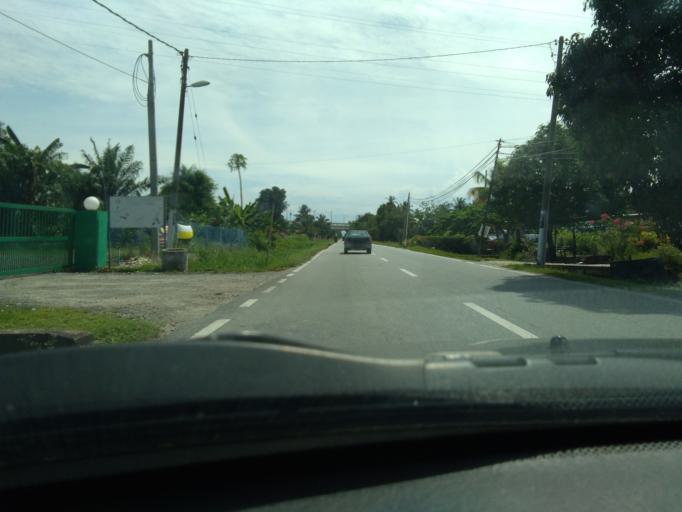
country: MY
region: Perak
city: Bagan Serai
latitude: 5.0171
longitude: 100.5427
